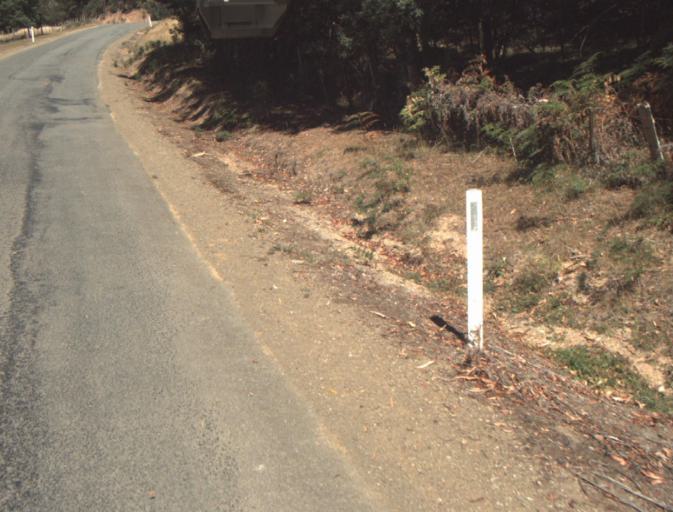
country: AU
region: Tasmania
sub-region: Dorset
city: Scottsdale
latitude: -41.3102
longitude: 147.3973
